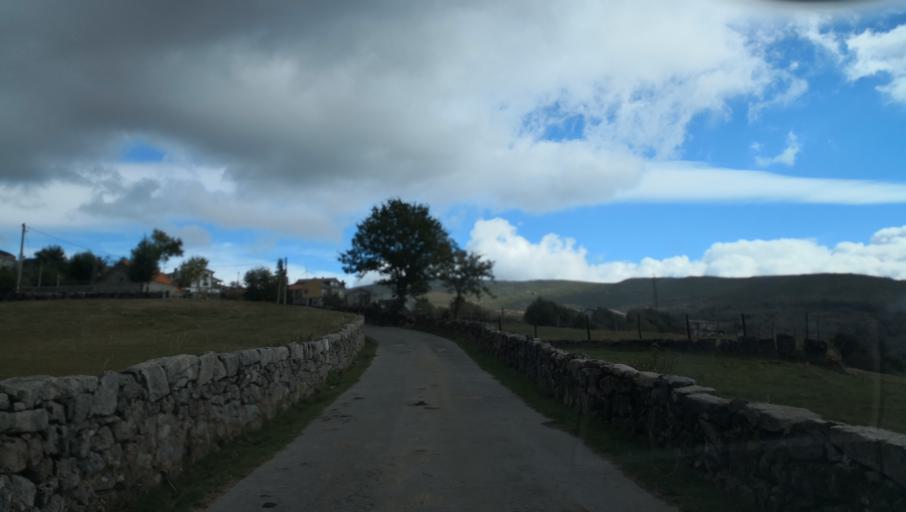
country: PT
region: Vila Real
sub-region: Vila Real
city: Vila Real
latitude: 41.3708
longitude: -7.7997
